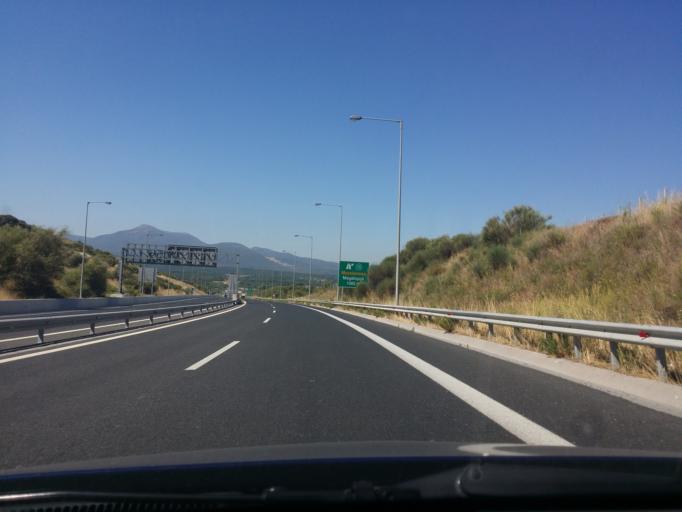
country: GR
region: Peloponnese
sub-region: Nomos Arkadias
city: Megalopoli
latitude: 37.3924
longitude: 22.1735
